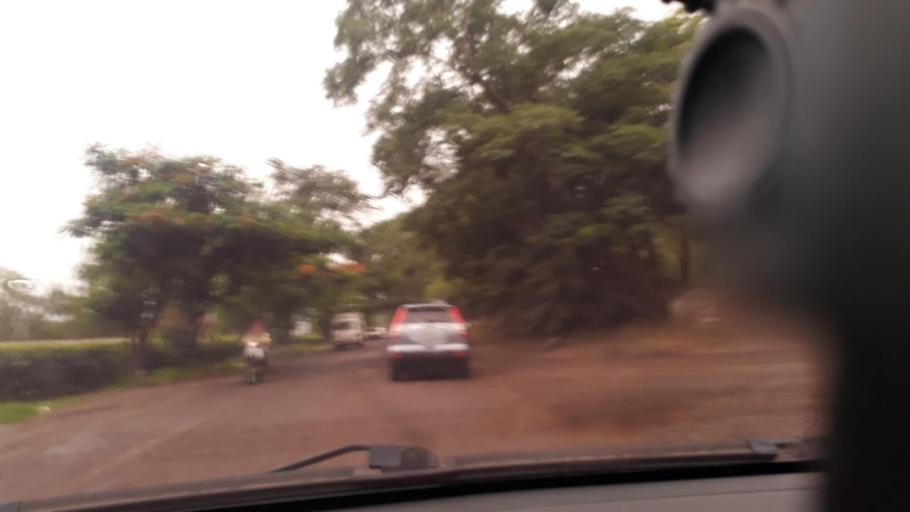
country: GT
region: Jutiapa
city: Asuncion Mita
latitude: 14.3105
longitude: -89.7157
